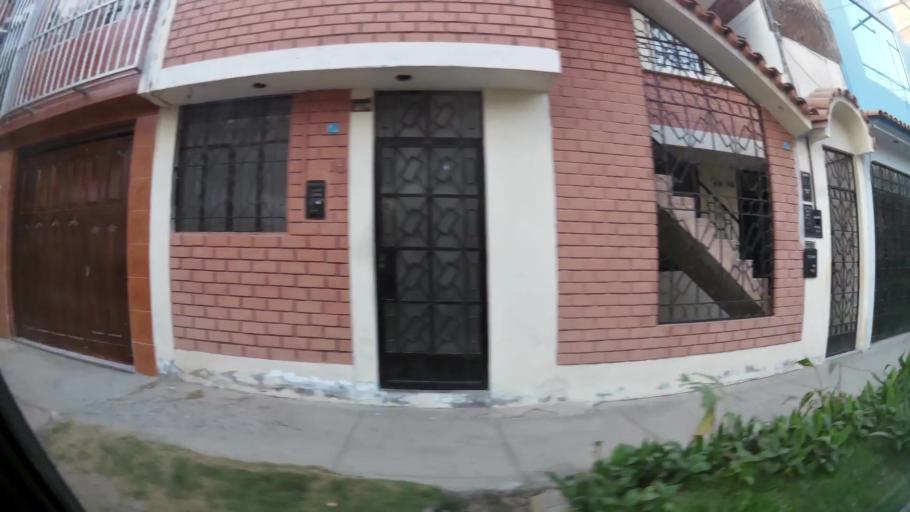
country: PE
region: Lambayeque
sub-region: Provincia de Chiclayo
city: Santa Rosa
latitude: -6.7681
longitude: -79.8337
